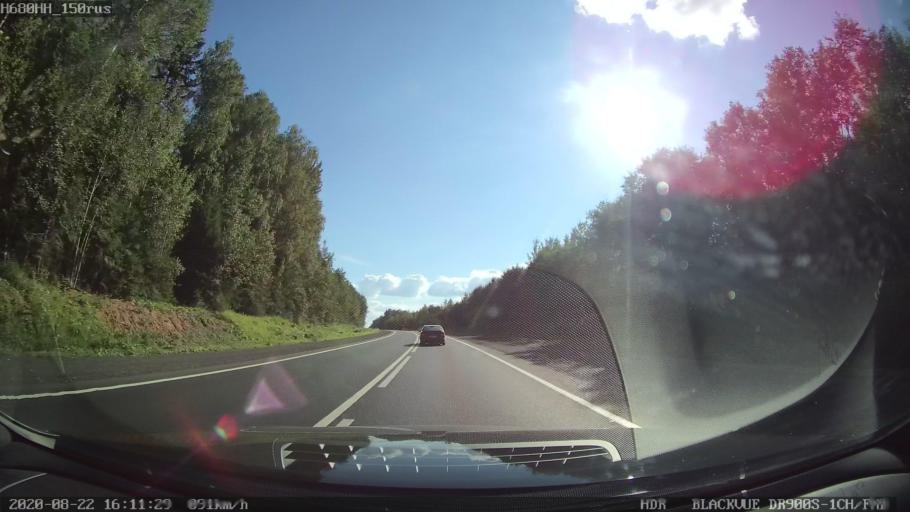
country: RU
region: Tverskaya
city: Rameshki
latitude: 57.5010
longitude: 36.2600
